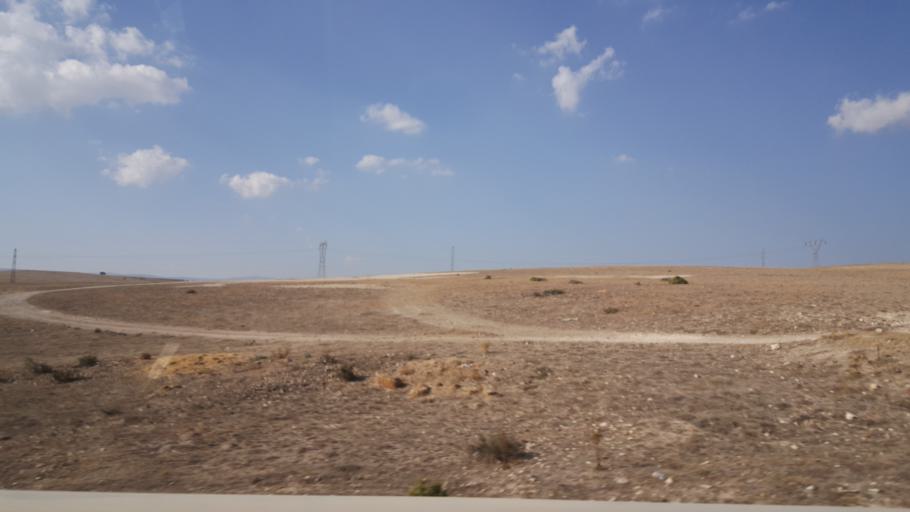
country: TR
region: Eskisehir
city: Kirka
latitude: 39.3220
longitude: 30.5580
